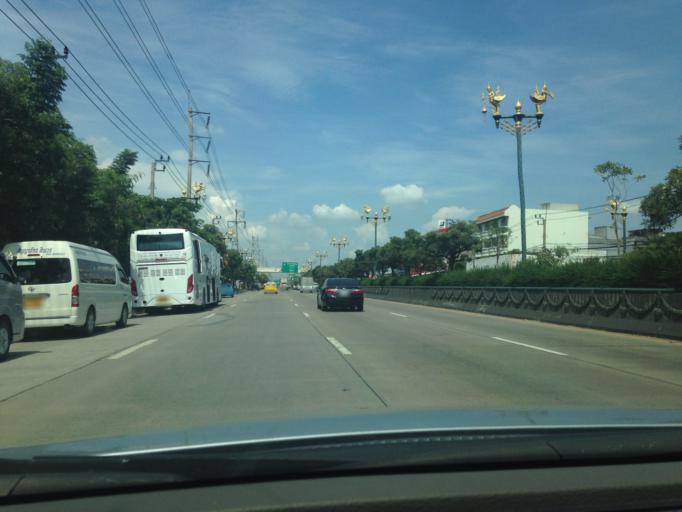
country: TH
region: Bangkok
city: Lat Krabang
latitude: 13.7047
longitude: 100.7350
